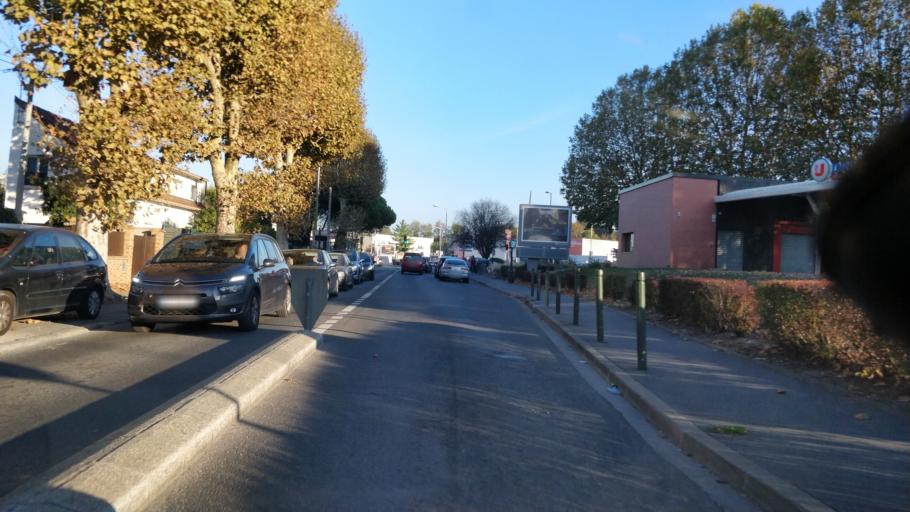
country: FR
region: Ile-de-France
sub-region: Departement de Seine-Saint-Denis
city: Noisy-le-Grand
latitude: 48.8660
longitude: 2.5627
